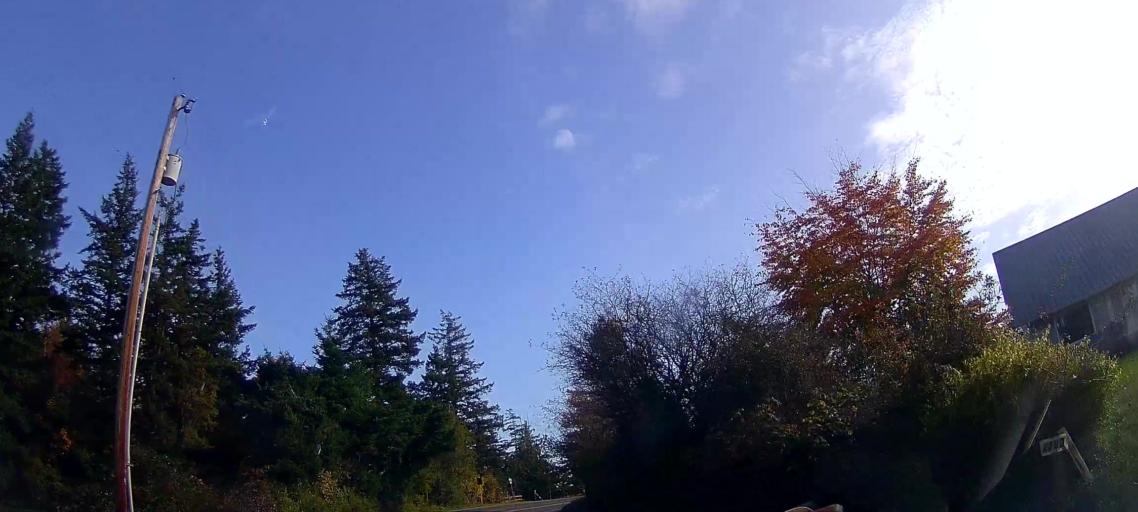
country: US
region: Washington
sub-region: Snohomish County
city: Stanwood
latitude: 48.2509
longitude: -122.4177
